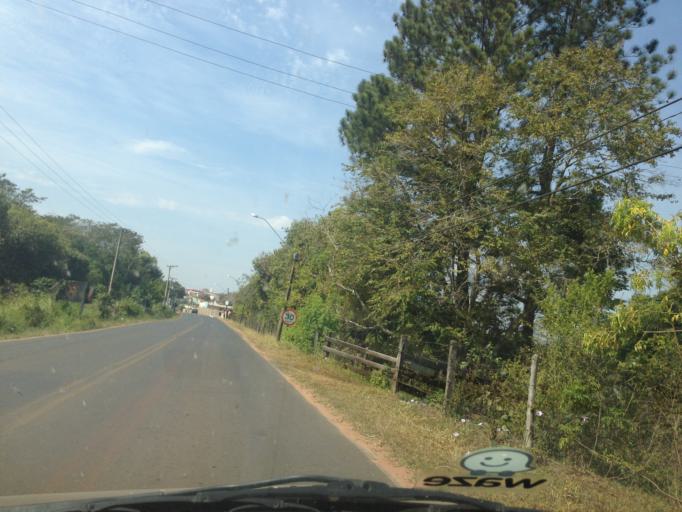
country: BR
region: Sao Paulo
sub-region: Casa Branca
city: Casa Branca
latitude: -21.7694
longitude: -47.0954
